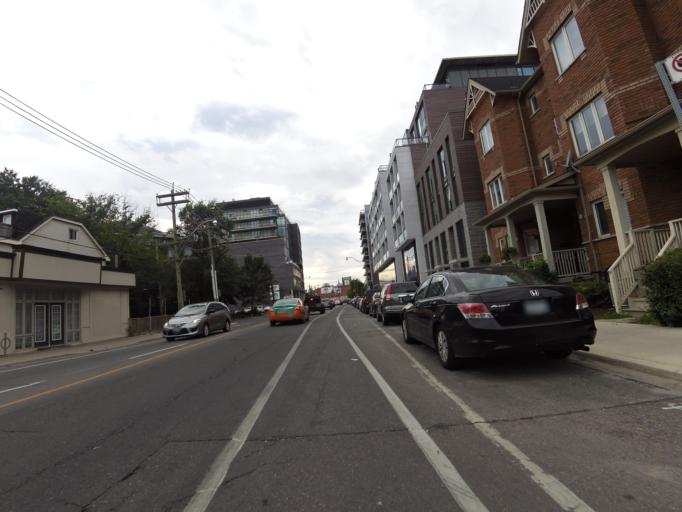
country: CA
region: Ontario
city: Toronto
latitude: 43.6653
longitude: -79.3398
